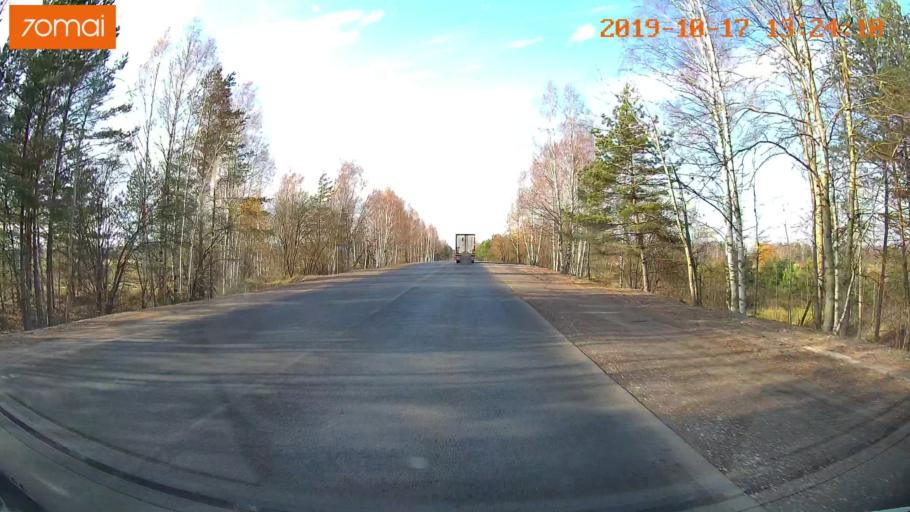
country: RU
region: Rjazan
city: Gus'-Zheleznyy
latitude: 55.0937
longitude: 40.9679
